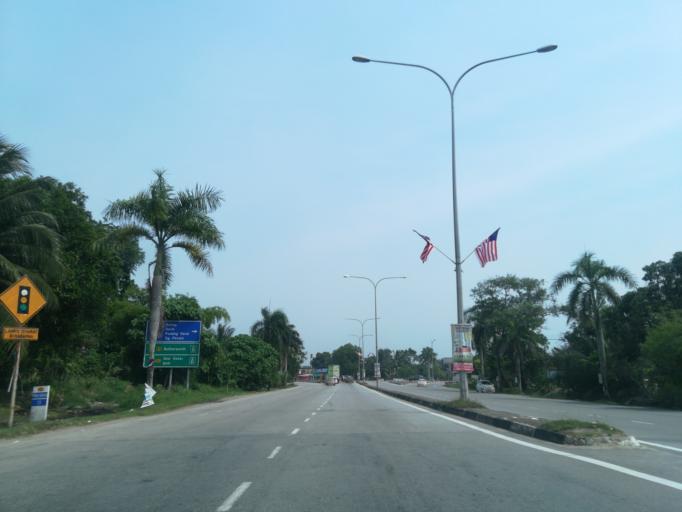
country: MY
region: Kedah
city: Kulim
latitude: 5.4317
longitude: 100.5519
